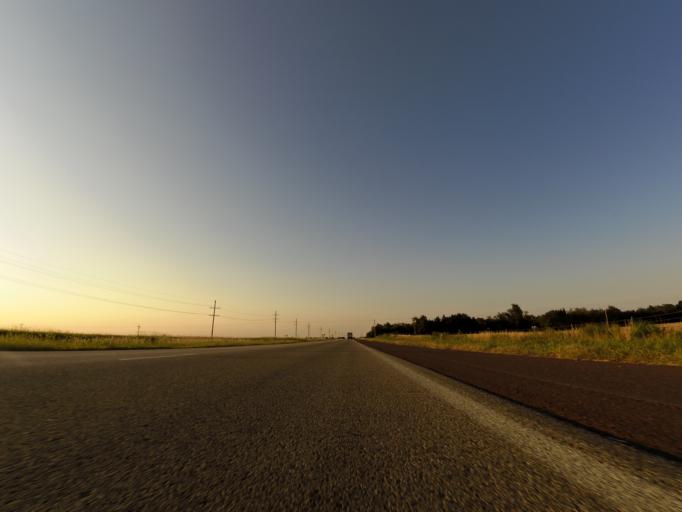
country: US
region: Kansas
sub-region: Reno County
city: South Hutchinson
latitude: 37.9827
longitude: -97.9403
